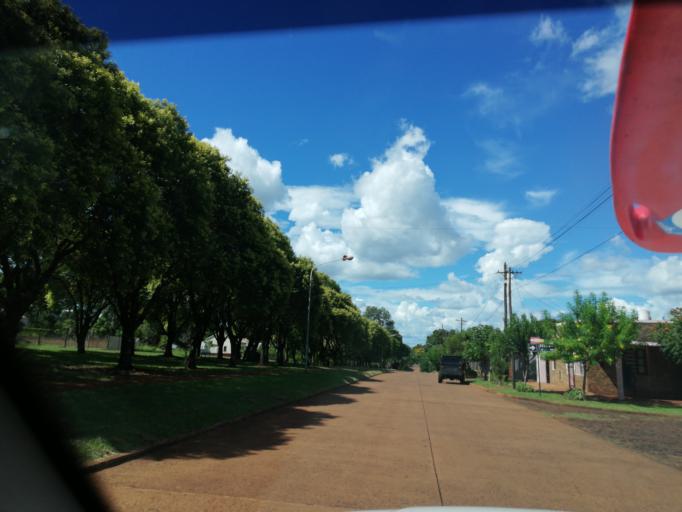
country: AR
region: Misiones
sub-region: Departamento de Apostoles
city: Apostoles
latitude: -27.9134
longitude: -55.7466
